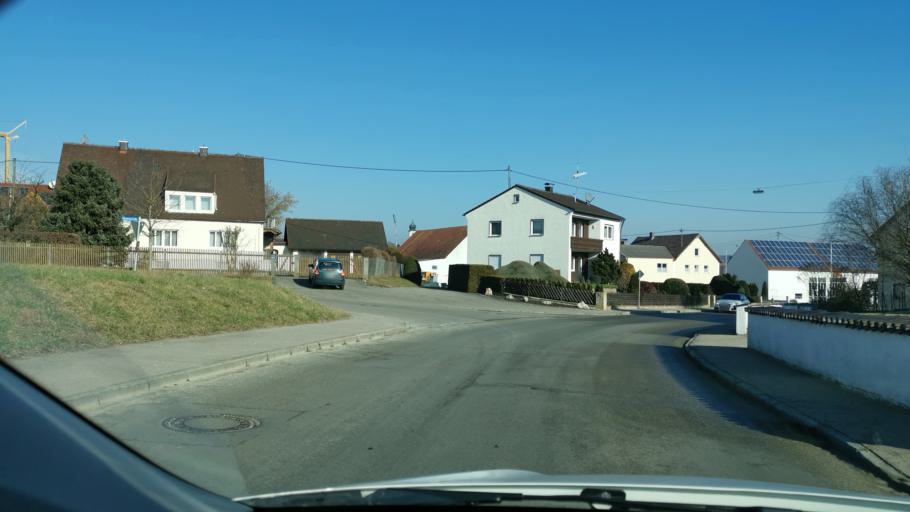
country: DE
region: Bavaria
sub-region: Swabia
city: Holzheim
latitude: 48.6091
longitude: 10.9488
